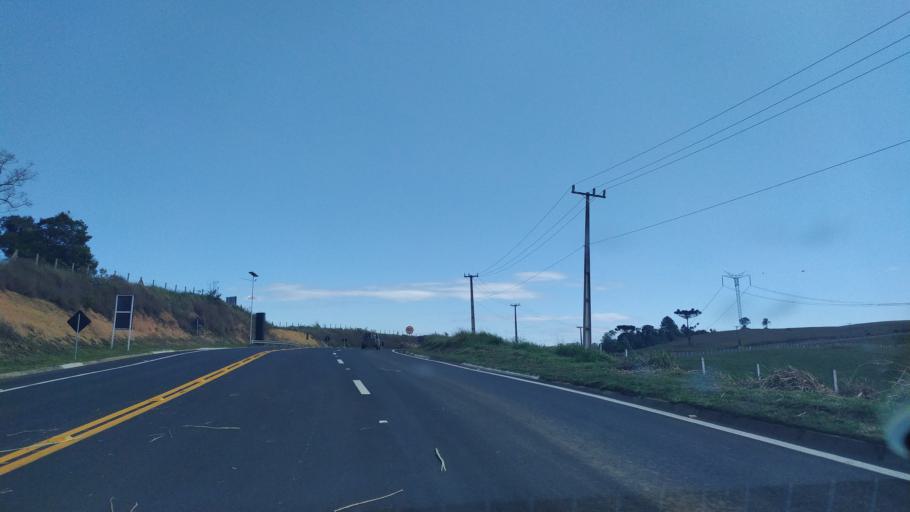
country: BR
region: Parana
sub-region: Telemaco Borba
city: Telemaco Borba
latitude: -24.2853
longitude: -50.7065
